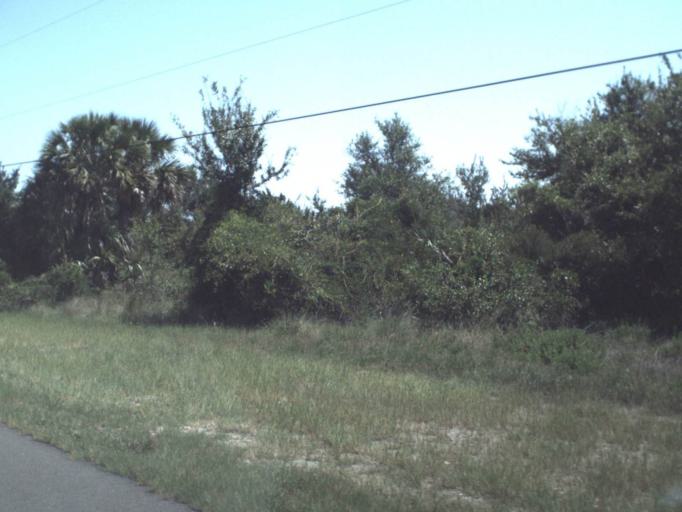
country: US
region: Florida
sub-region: Duval County
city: Atlantic Beach
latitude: 30.4326
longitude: -81.4131
